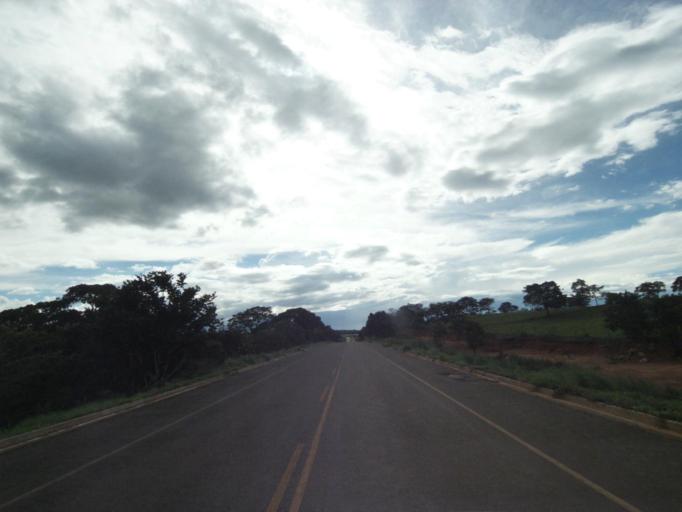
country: BR
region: Goias
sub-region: Jaragua
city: Jaragua
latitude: -15.8428
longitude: -49.3371
